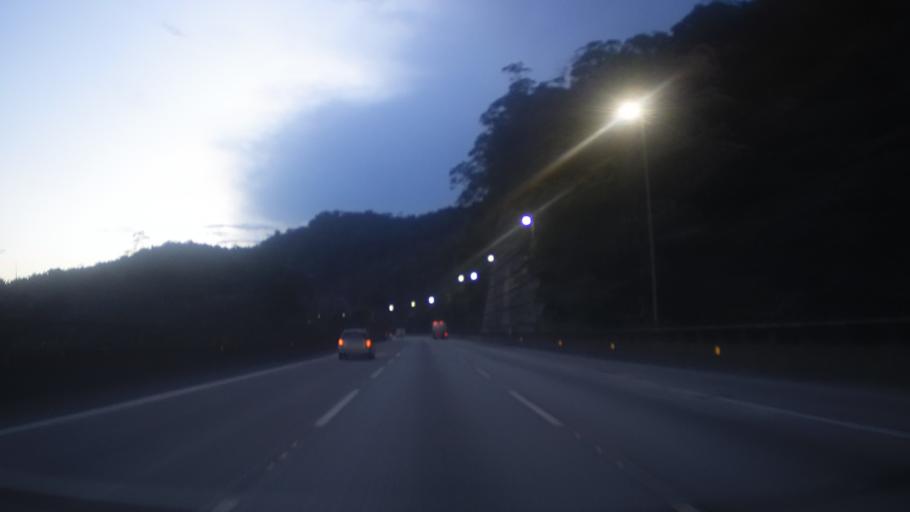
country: BR
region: Sao Paulo
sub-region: Cubatao
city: Cubatao
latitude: -23.9175
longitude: -46.5275
